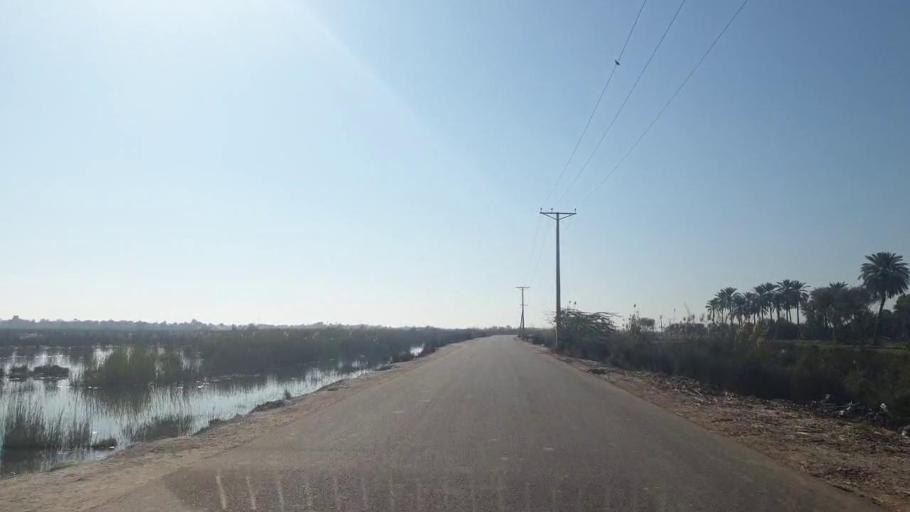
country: PK
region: Sindh
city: Kot Diji
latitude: 27.3160
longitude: 68.6492
